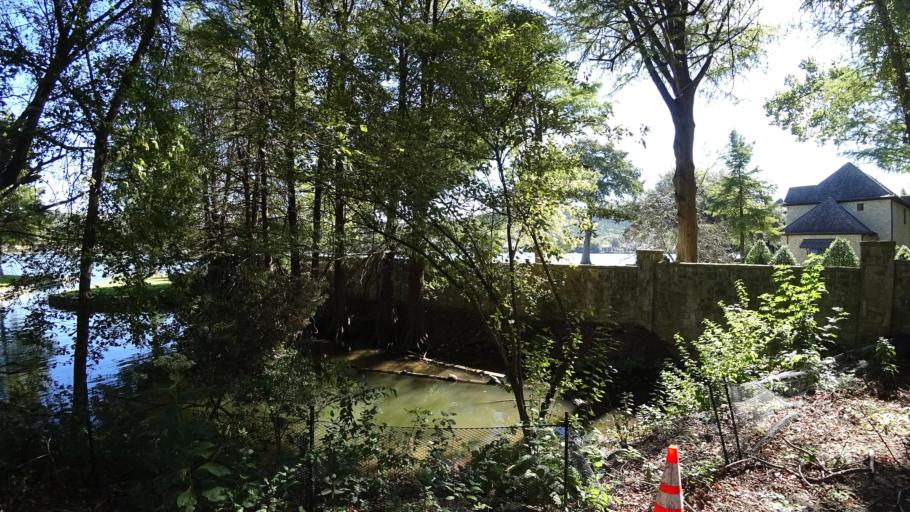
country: US
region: Texas
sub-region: Travis County
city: West Lake Hills
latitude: 30.3328
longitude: -97.7832
